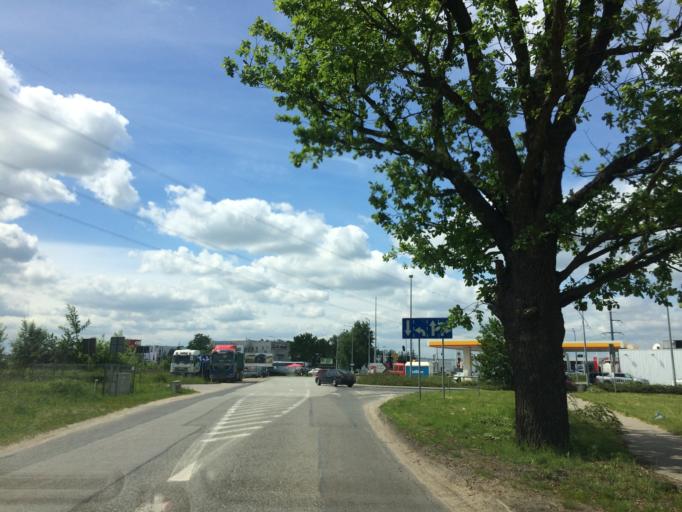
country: PL
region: Lower Silesian Voivodeship
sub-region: Powiat wroclawski
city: Dlugoleka
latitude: 51.1740
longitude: 17.1806
